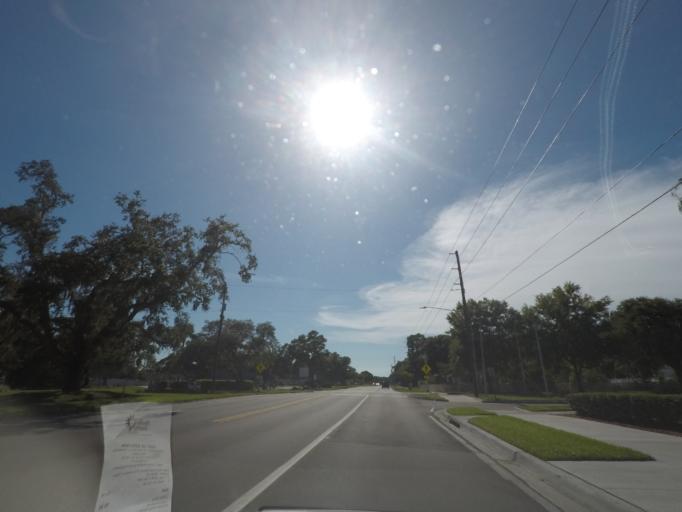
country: US
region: Florida
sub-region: Pinellas County
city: Gulfport
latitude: 27.7483
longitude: -82.7076
